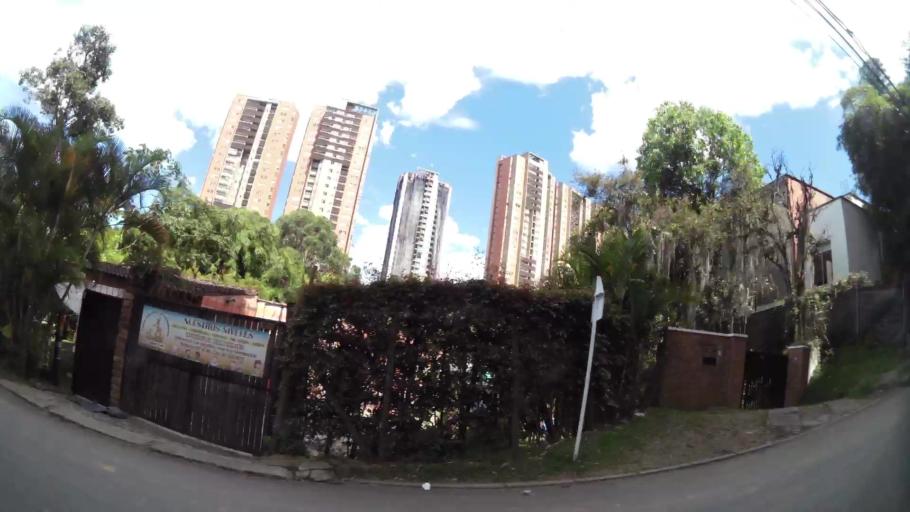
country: CO
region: Antioquia
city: Sabaneta
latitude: 6.1435
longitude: -75.6213
